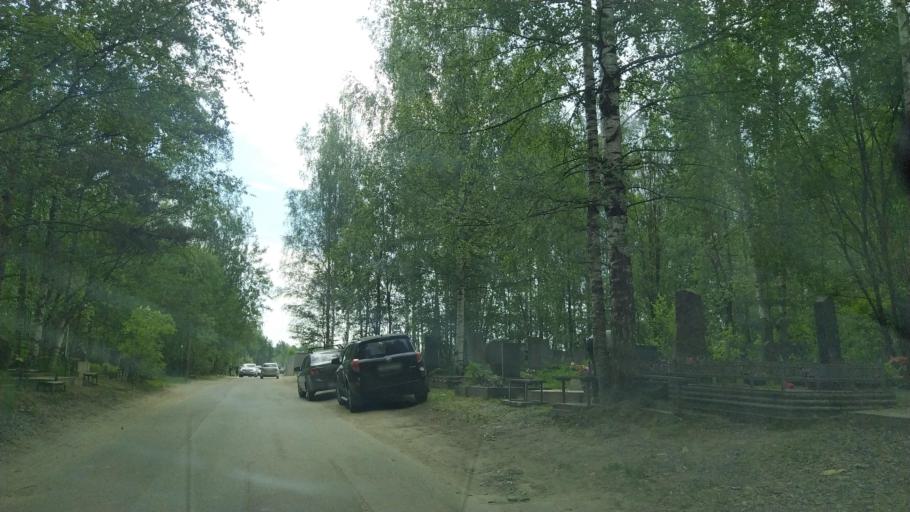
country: RU
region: St.-Petersburg
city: Aleksandrovskaya
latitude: 59.7643
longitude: 30.2628
